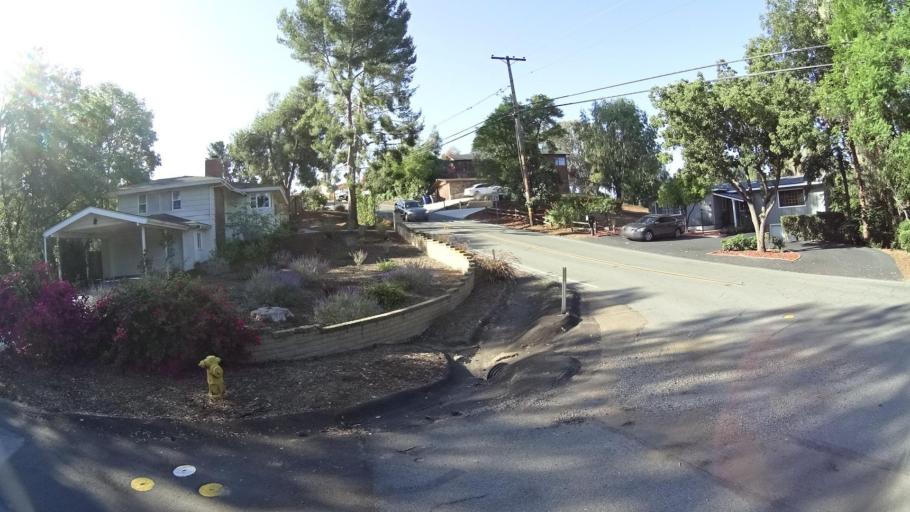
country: US
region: California
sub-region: San Diego County
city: Spring Valley
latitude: 32.7652
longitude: -116.9968
